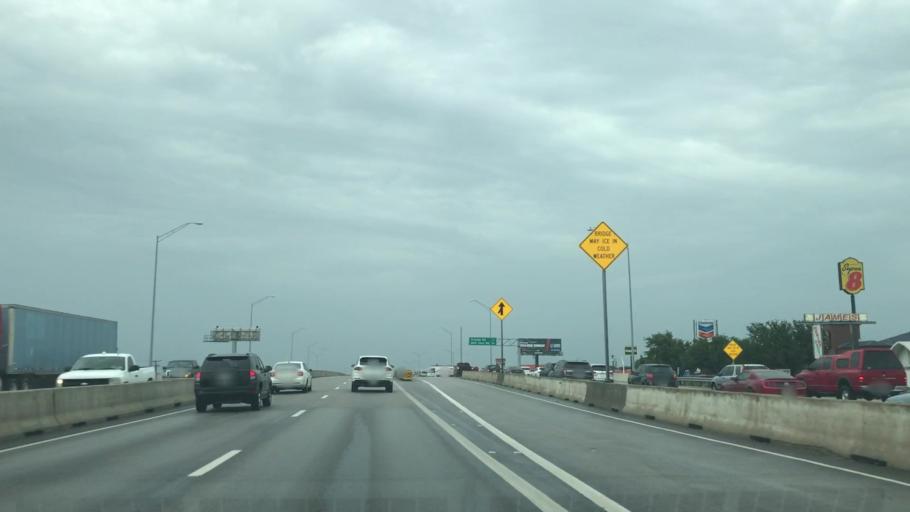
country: US
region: Texas
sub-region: Dallas County
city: Carrollton
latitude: 32.9472
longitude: -96.9030
